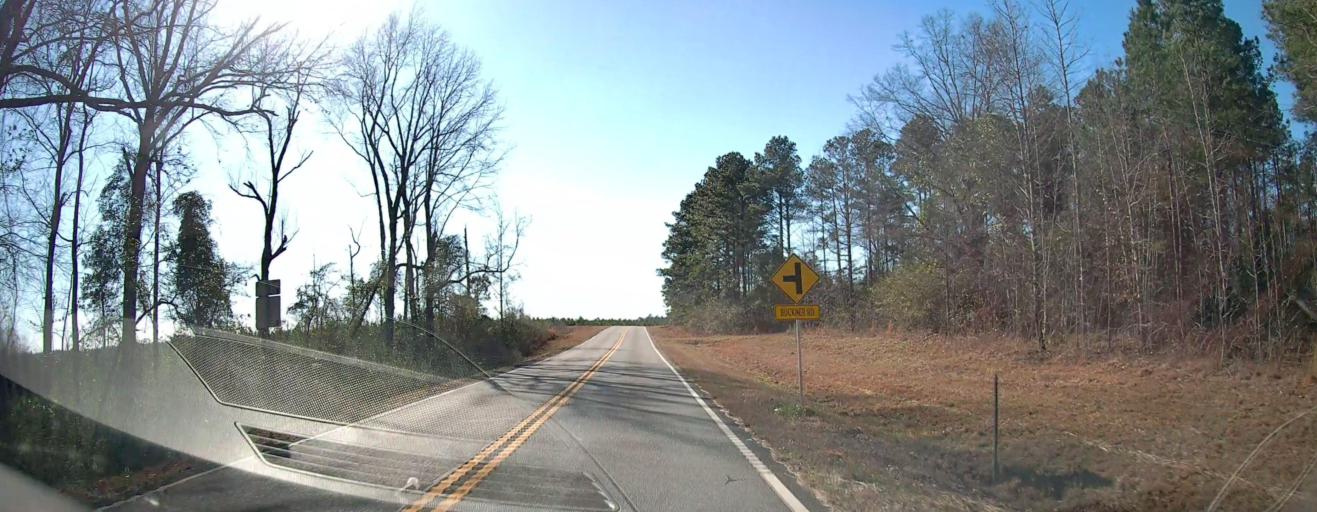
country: US
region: Georgia
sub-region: Talbot County
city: Talbotton
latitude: 32.6461
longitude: -84.4164
